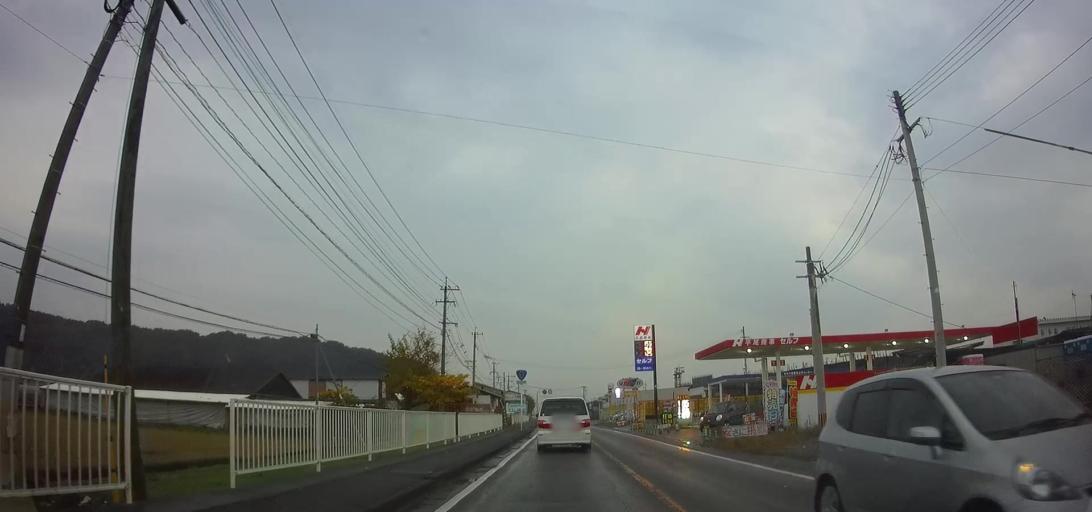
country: JP
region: Nagasaki
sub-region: Isahaya-shi
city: Isahaya
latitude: 32.8356
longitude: 130.1091
